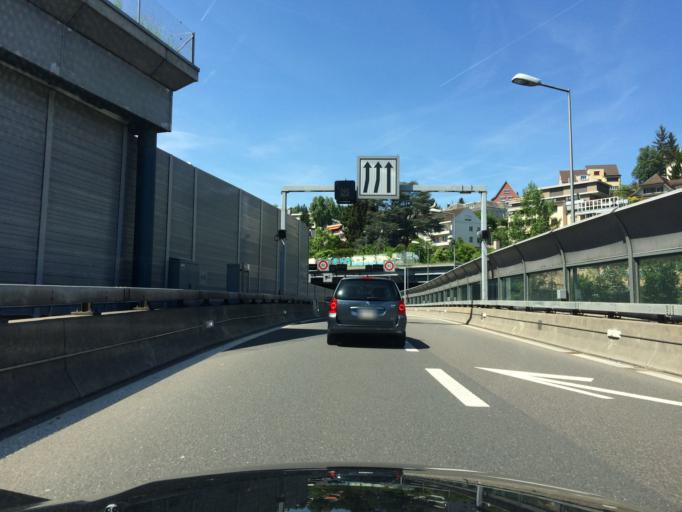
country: CH
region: Lucerne
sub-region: Lucerne-Stadt District
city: Luzern
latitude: 47.0542
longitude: 8.2969
